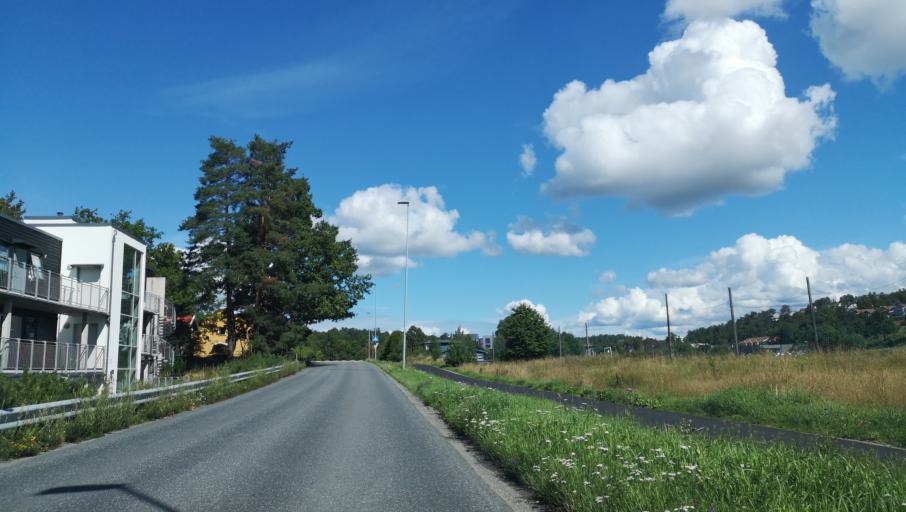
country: NO
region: Akershus
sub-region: Frogn
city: Drobak
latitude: 59.6644
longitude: 10.6404
